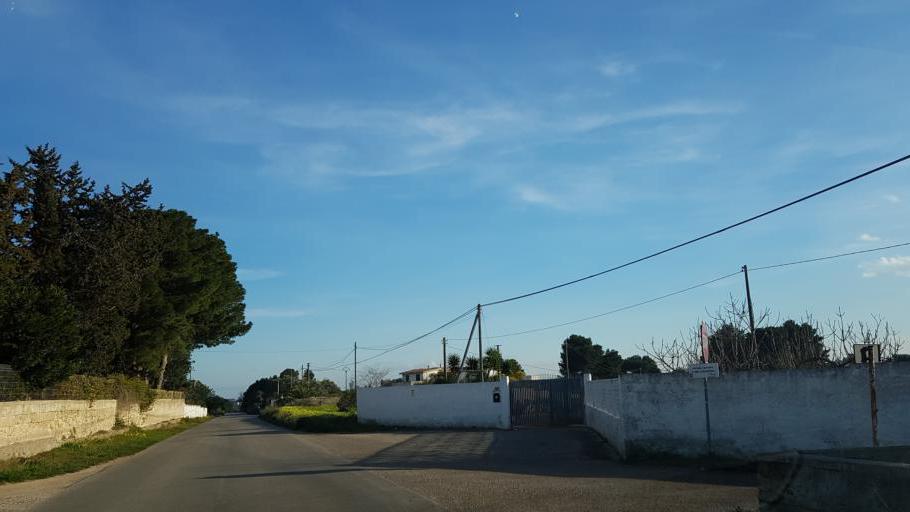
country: IT
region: Apulia
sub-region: Provincia di Brindisi
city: San Vito dei Normanni
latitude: 40.6820
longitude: 17.7698
